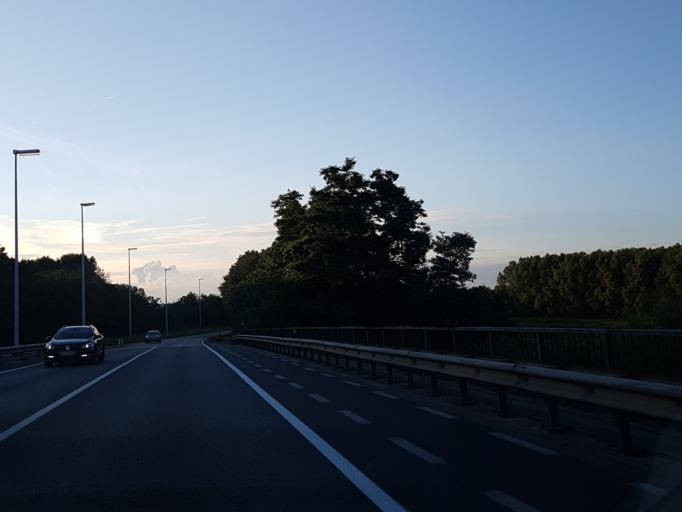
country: BE
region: Flanders
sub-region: Provincie Oost-Vlaanderen
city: Dendermonde
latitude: 51.0416
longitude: 4.1231
